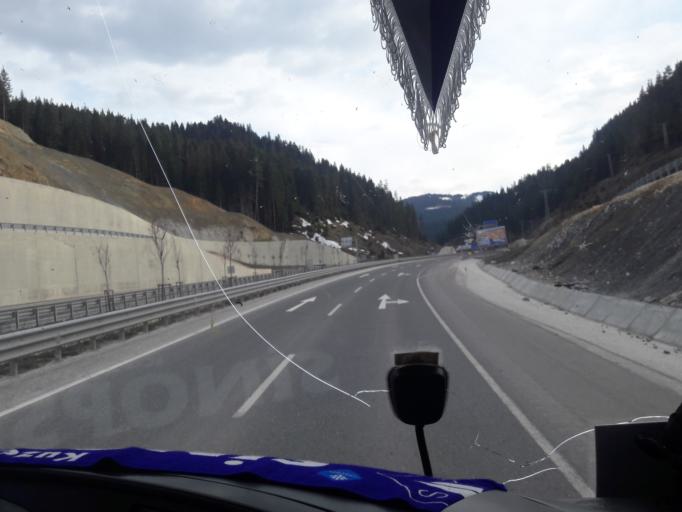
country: TR
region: Kastamonu
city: Kuzyaka
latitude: 41.1006
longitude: 33.7512
